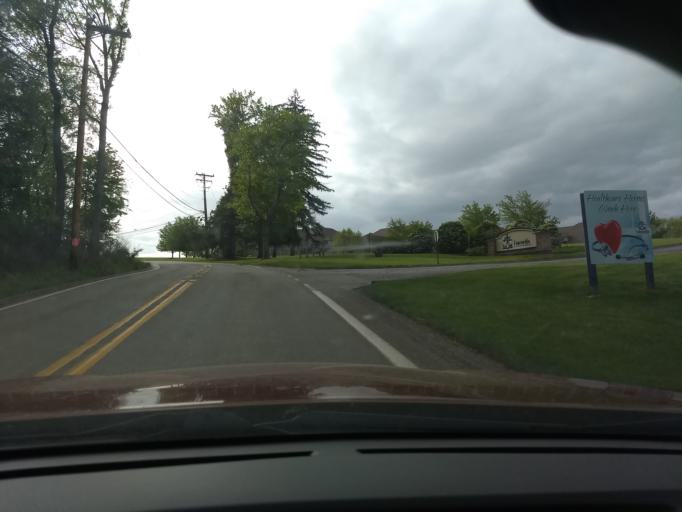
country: US
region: Pennsylvania
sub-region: Allegheny County
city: Russellton
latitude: 40.6013
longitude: -79.8967
